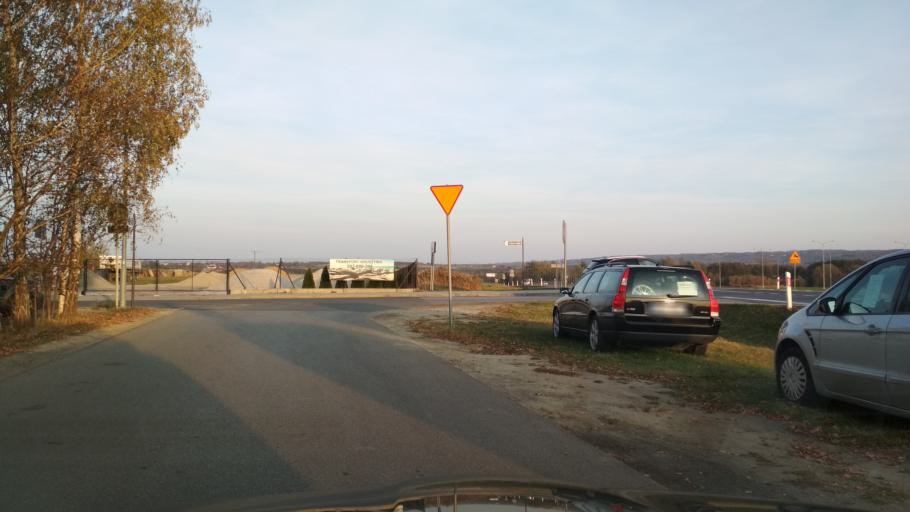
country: PL
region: Subcarpathian Voivodeship
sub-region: Powiat ropczycko-sedziszowski
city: Sedziszow Malopolski
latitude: 50.0625
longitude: 21.7137
